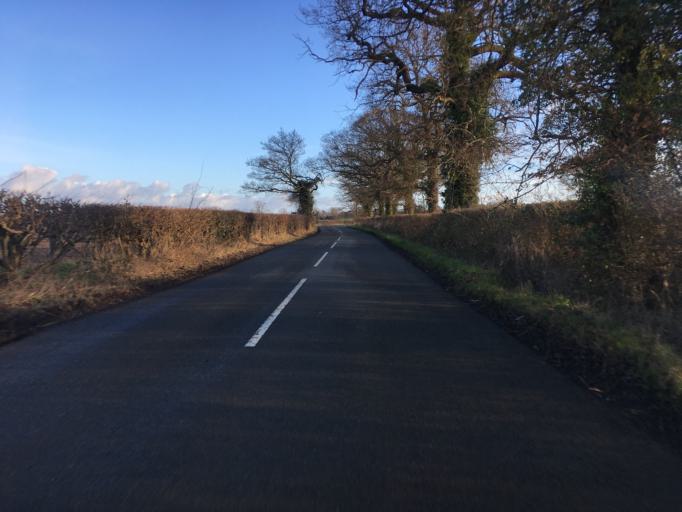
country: GB
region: England
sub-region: Warwickshire
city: Henley in Arden
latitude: 52.2465
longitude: -1.7900
